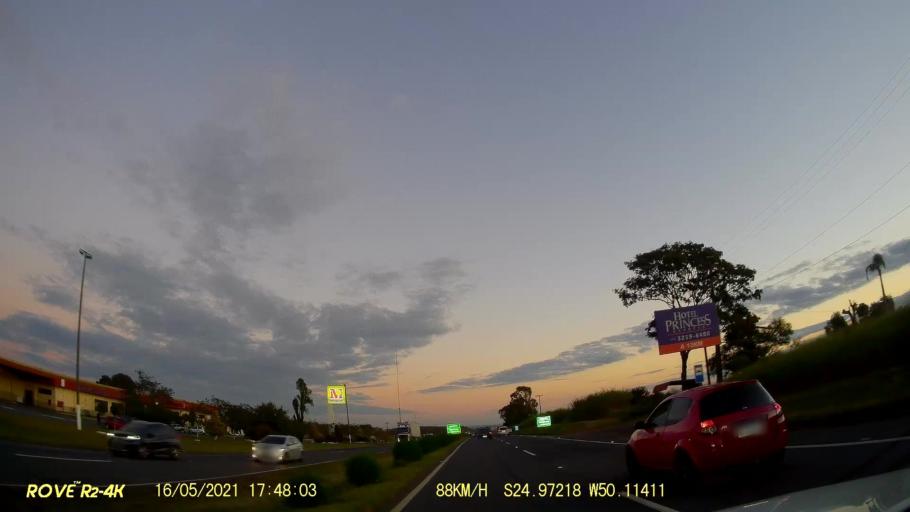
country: BR
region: Parana
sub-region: Carambei
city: Carambei
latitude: -24.9722
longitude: -50.1141
